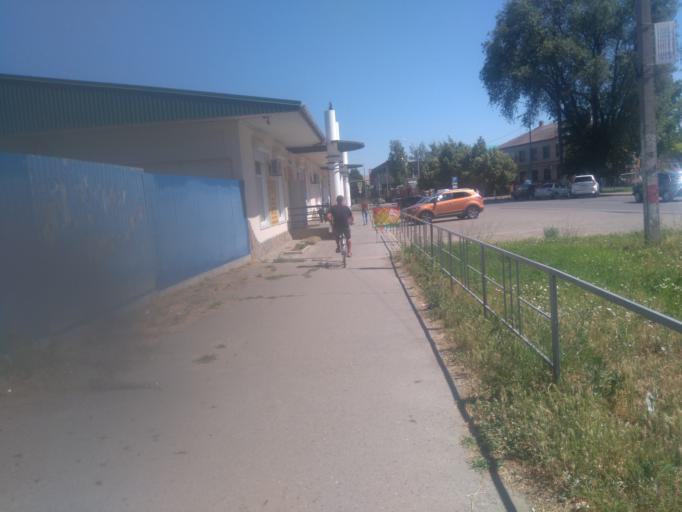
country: RU
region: Krasnodarskiy
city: Fastovetskaya
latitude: 45.9188
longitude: 40.1555
